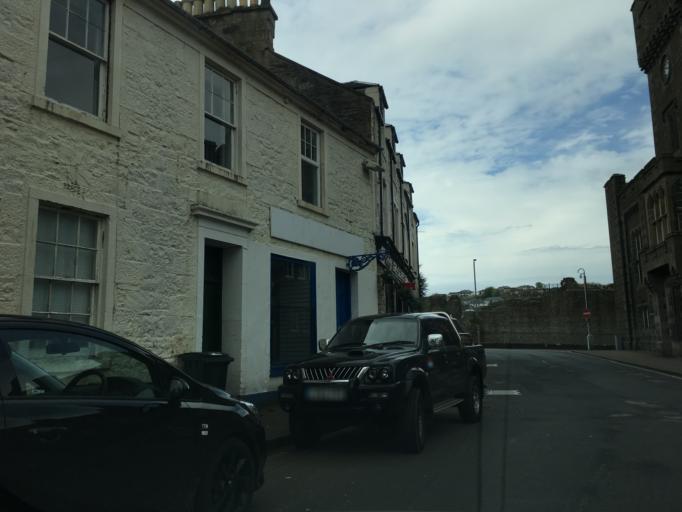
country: GB
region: Scotland
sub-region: Argyll and Bute
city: Rothesay
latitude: 55.8362
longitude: -5.0532
